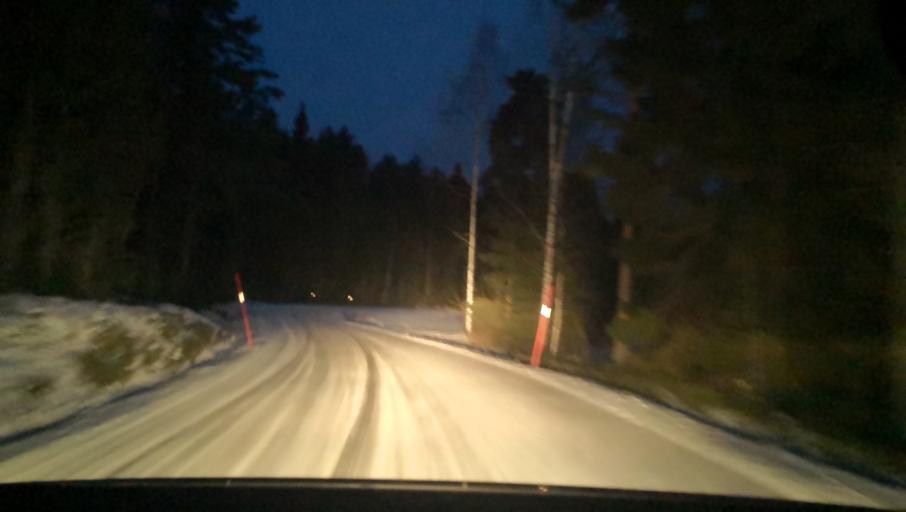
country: SE
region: Uppsala
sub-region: Heby Kommun
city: Tarnsjo
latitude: 60.2579
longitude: 16.7743
